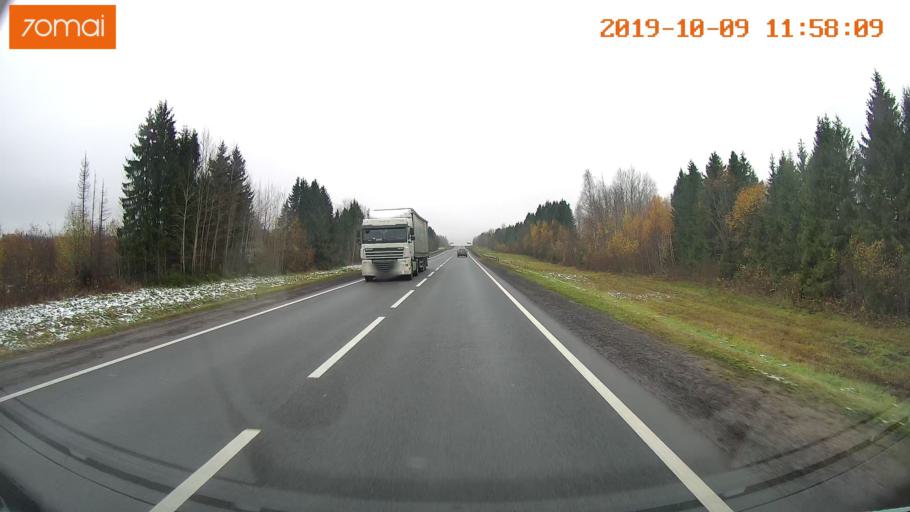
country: RU
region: Vologda
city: Gryazovets
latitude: 58.7223
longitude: 40.2961
